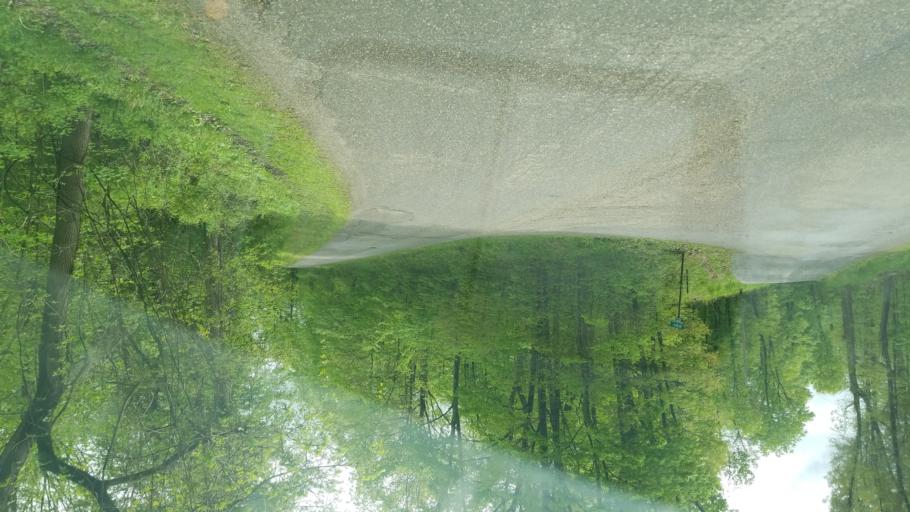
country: US
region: Ohio
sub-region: Tuscarawas County
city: Rockford
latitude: 40.4550
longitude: -81.2777
